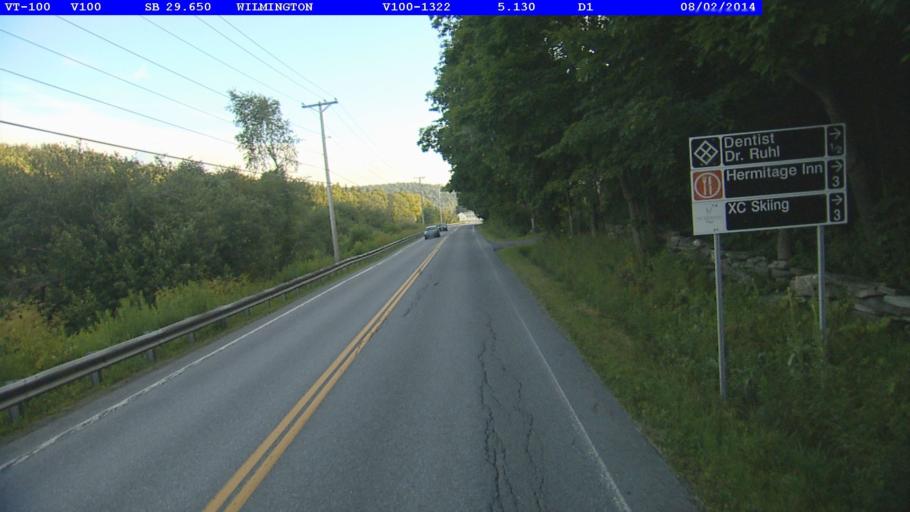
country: US
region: Vermont
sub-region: Windham County
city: Dover
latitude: 42.9002
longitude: -72.8544
